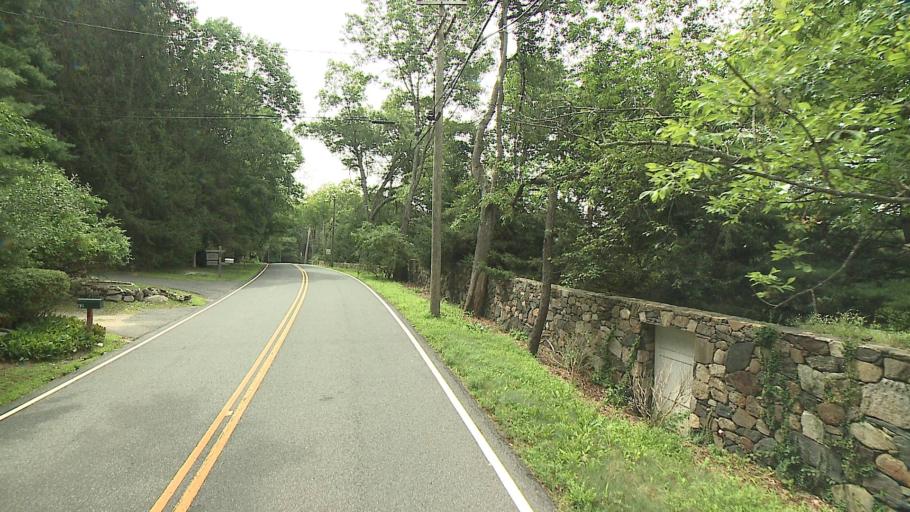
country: US
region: Connecticut
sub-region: Litchfield County
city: New Preston
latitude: 41.6198
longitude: -73.3185
